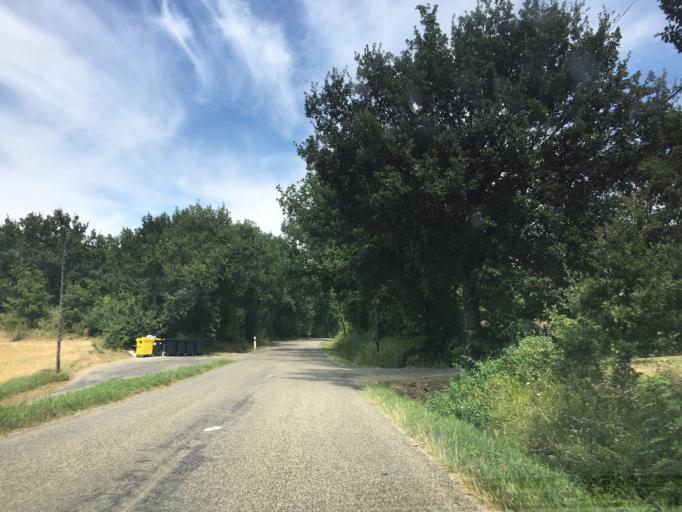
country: FR
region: Midi-Pyrenees
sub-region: Departement du Gers
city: Fleurance
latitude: 43.8300
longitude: 0.6394
